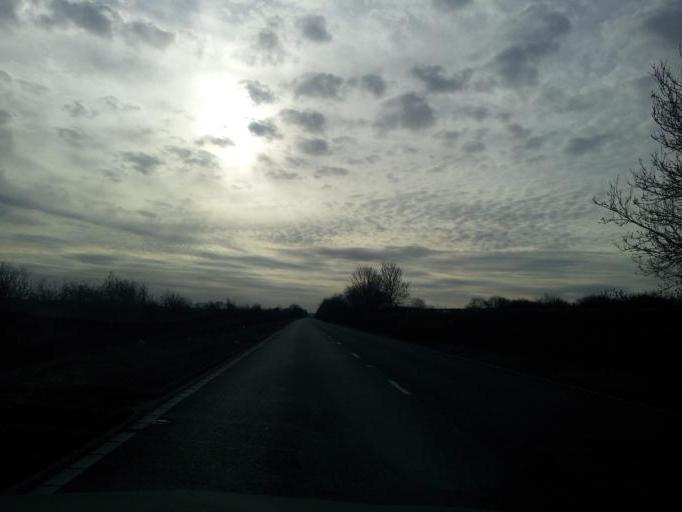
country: GB
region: England
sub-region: District of Rutland
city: Tickencote
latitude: 52.6856
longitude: -0.5518
